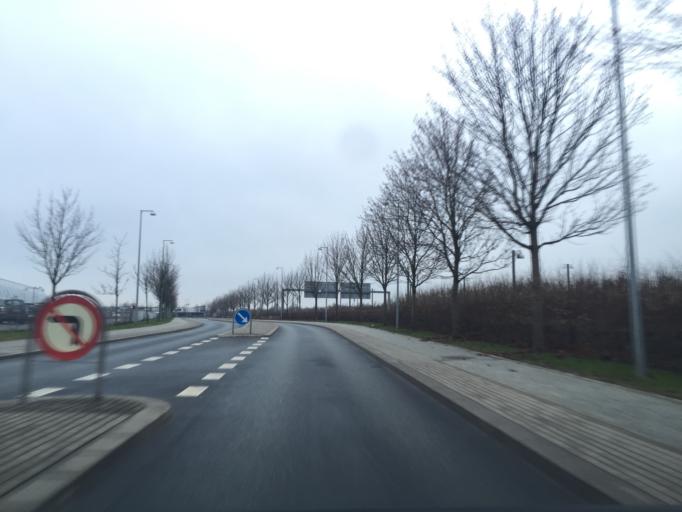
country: DK
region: Capital Region
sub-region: Tarnby Kommune
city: Tarnby
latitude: 55.6299
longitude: 12.6380
